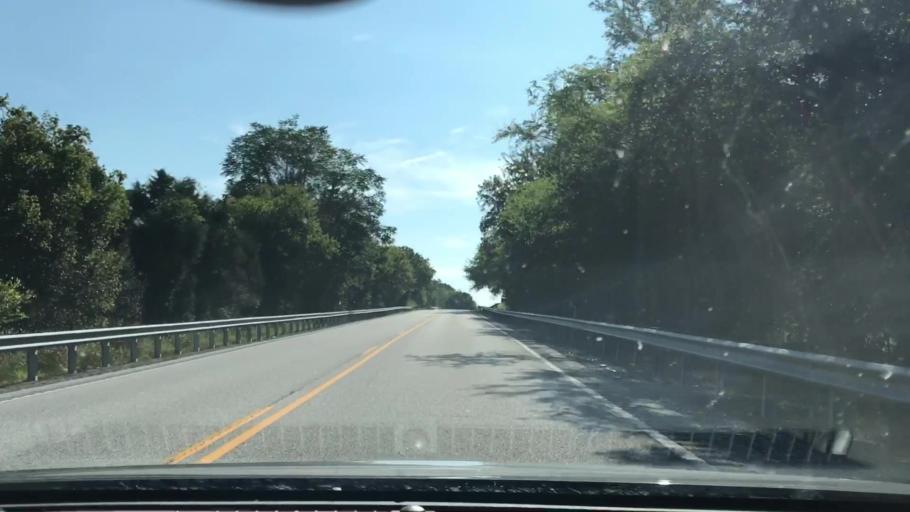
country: US
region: Tennessee
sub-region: Jackson County
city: Gainesboro
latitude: 36.3577
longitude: -85.7335
